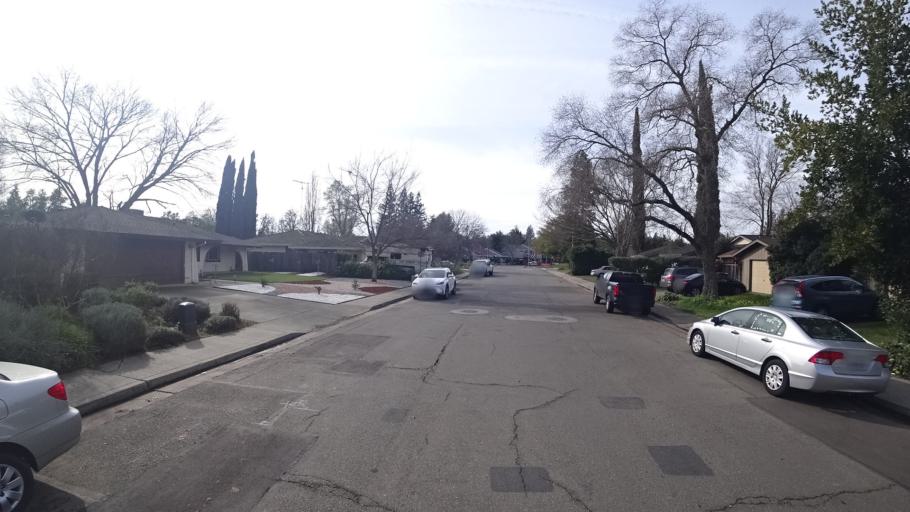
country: US
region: California
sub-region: Yolo County
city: Davis
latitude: 38.5504
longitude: -121.6892
